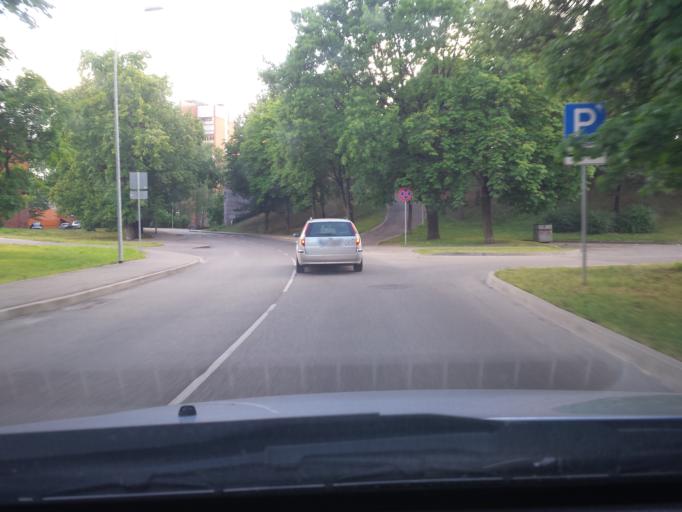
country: LV
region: Marupe
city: Marupe
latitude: 56.9611
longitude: 24.0339
